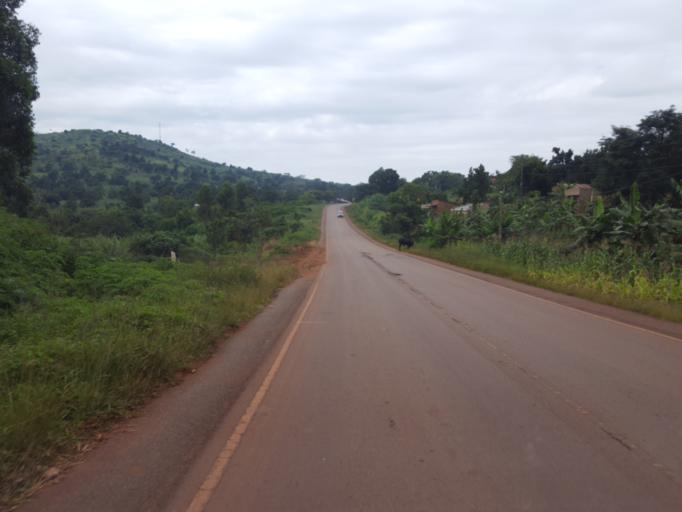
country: UG
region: Central Region
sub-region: Mityana District
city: Mityana
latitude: 0.6563
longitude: 32.0932
